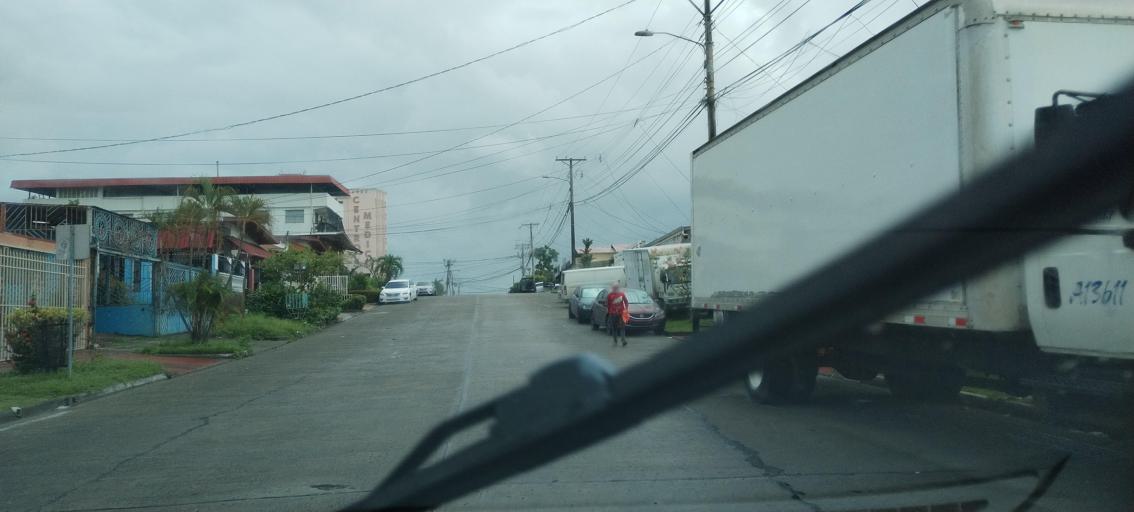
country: PA
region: Panama
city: San Miguelito
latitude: 9.0362
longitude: -79.4847
